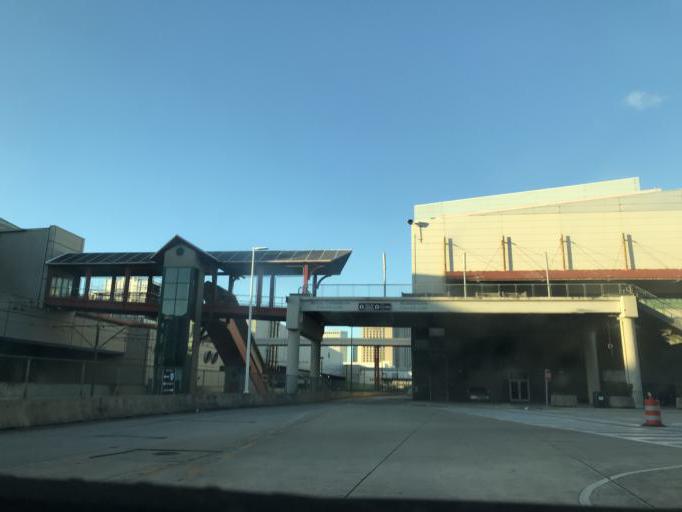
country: US
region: Louisiana
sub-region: Orleans Parish
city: New Orleans
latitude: 29.9408
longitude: -90.0619
